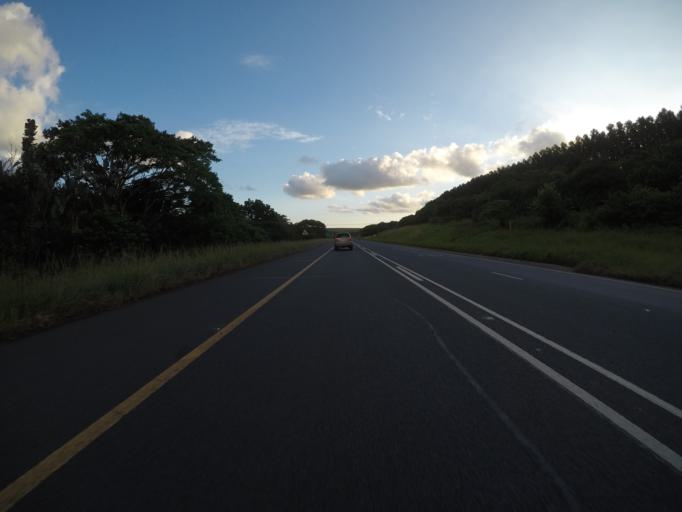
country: ZA
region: KwaZulu-Natal
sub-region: uThungulu District Municipality
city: Richards Bay
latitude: -28.6848
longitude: 32.0402
